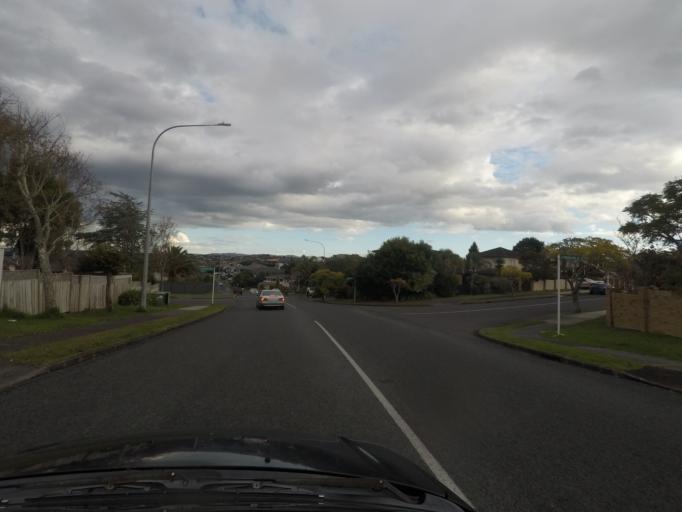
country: NZ
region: Auckland
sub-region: Auckland
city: Rosebank
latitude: -36.8057
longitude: 174.6420
